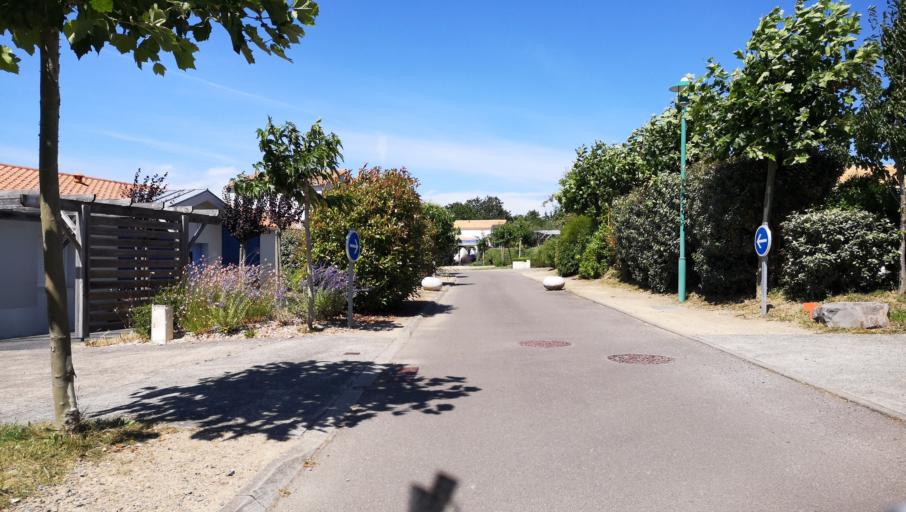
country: FR
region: Pays de la Loire
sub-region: Departement de la Vendee
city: Chateau-d'Olonne
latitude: 46.4773
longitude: -1.7325
